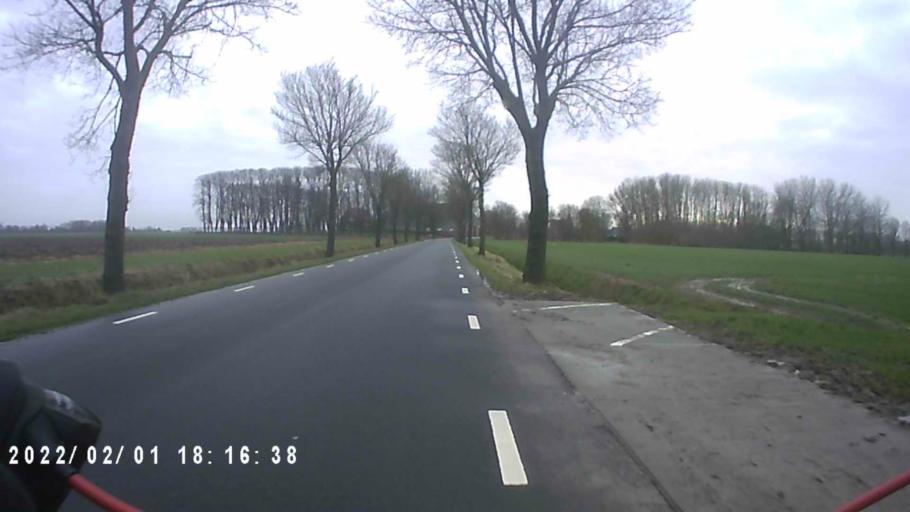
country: NL
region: Groningen
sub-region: Gemeente De Marne
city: Ulrum
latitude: 53.3452
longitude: 6.3317
